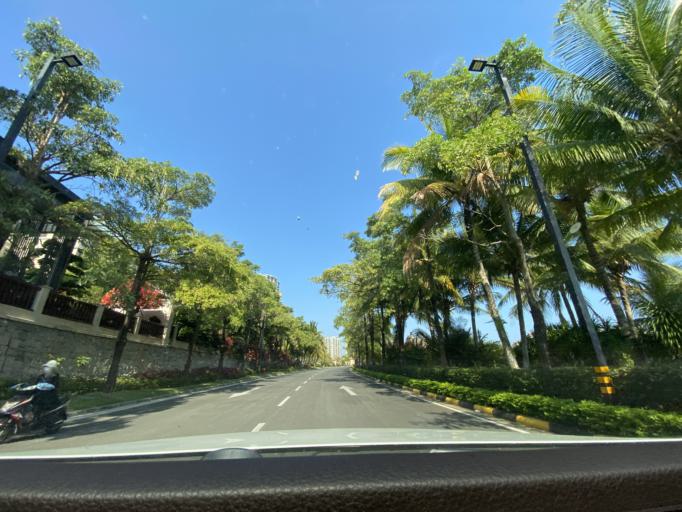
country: CN
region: Hainan
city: Yingzhou
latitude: 18.4099
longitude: 109.8784
